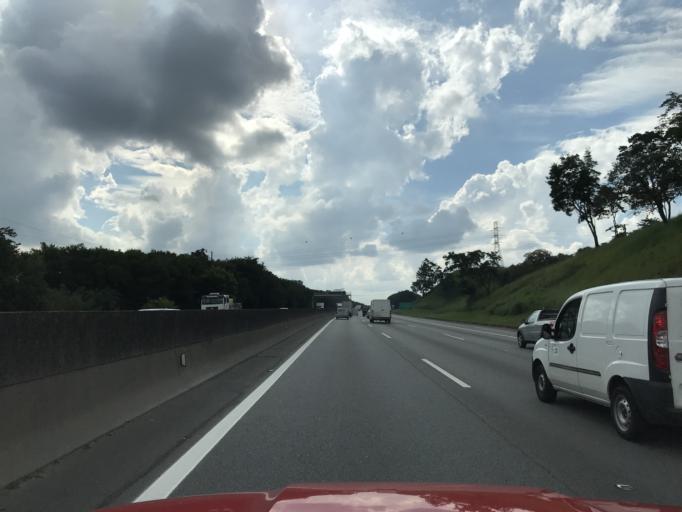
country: BR
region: Sao Paulo
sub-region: Jundiai
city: Jundiai
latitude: -23.1575
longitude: -46.9332
